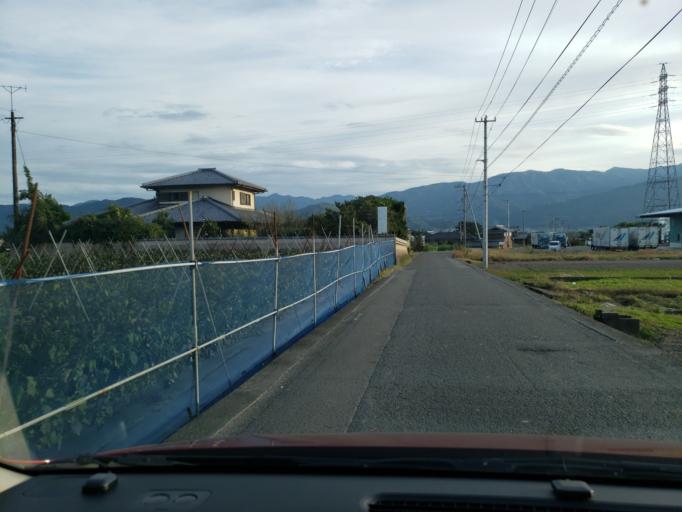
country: JP
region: Tokushima
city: Wakimachi
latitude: 34.0808
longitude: 134.2283
